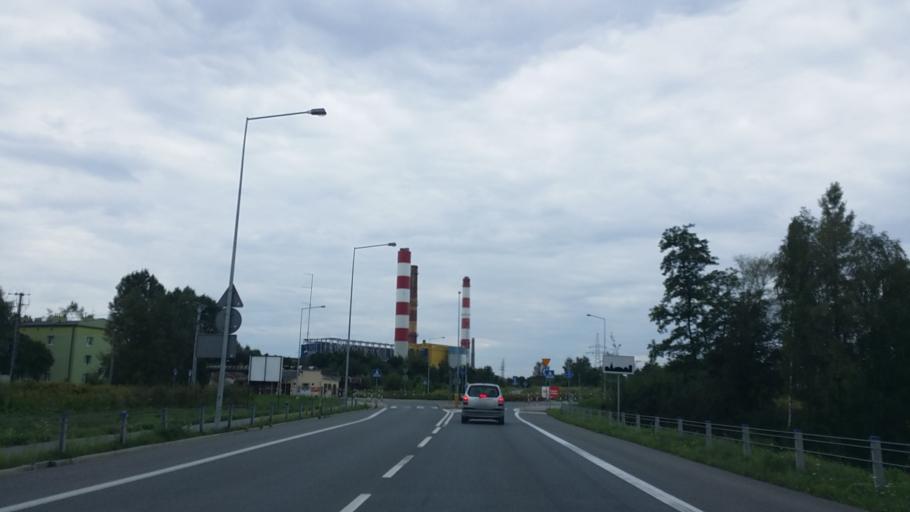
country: PL
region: Lesser Poland Voivodeship
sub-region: Powiat krakowski
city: Skawina
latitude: 49.9831
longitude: 19.8098
